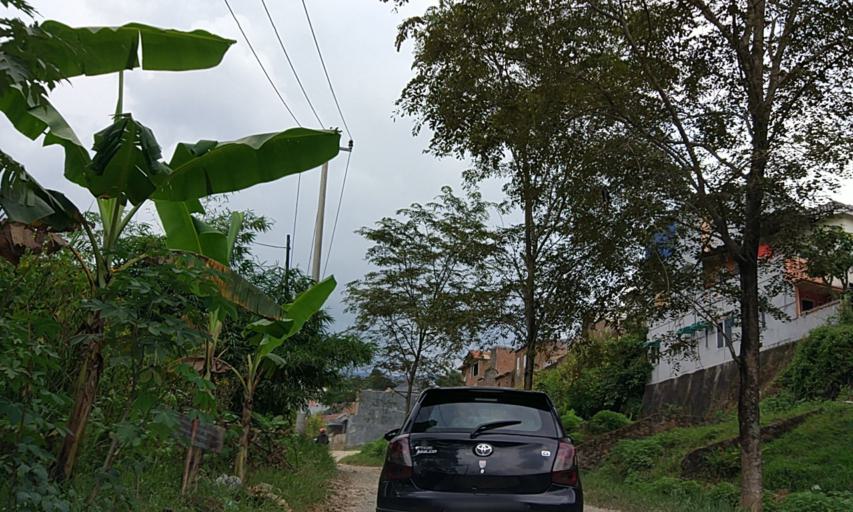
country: ID
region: West Java
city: Cileunyi
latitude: -6.9004
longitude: 107.6937
